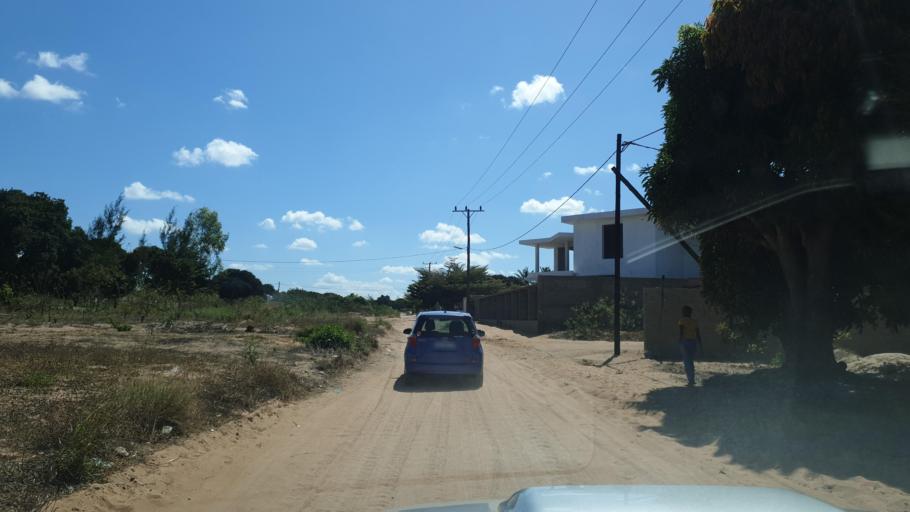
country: MZ
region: Nampula
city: Nampula
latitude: -15.1056
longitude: 39.2062
